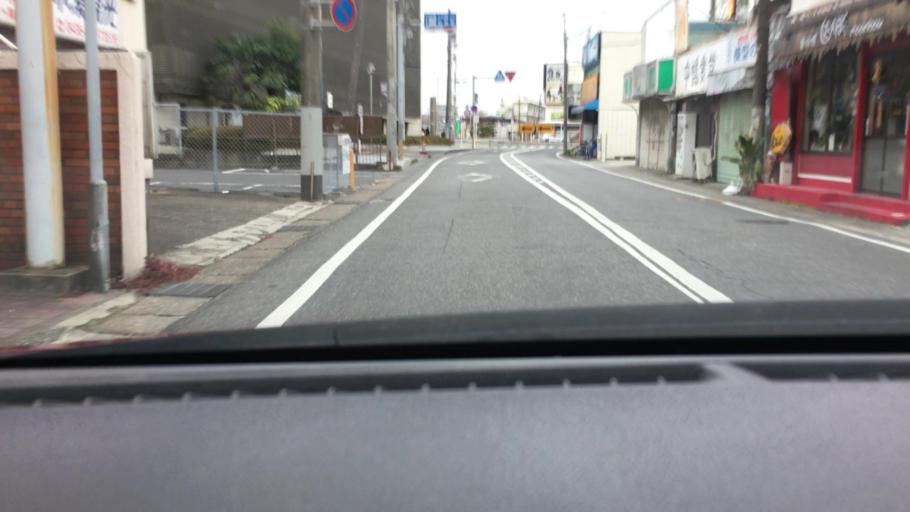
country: JP
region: Chiba
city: Kisarazu
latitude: 35.3827
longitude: 139.9256
